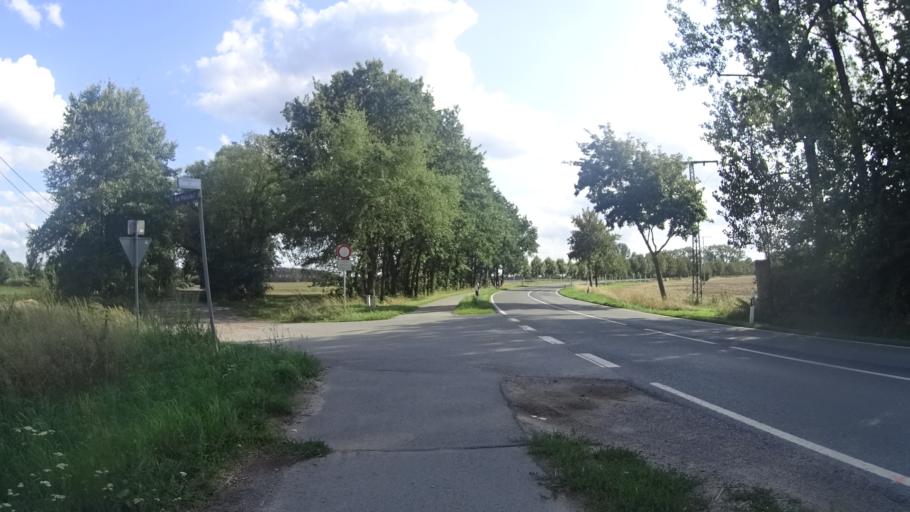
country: DE
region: Brandenburg
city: Rathenow
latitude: 52.6531
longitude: 12.3383
